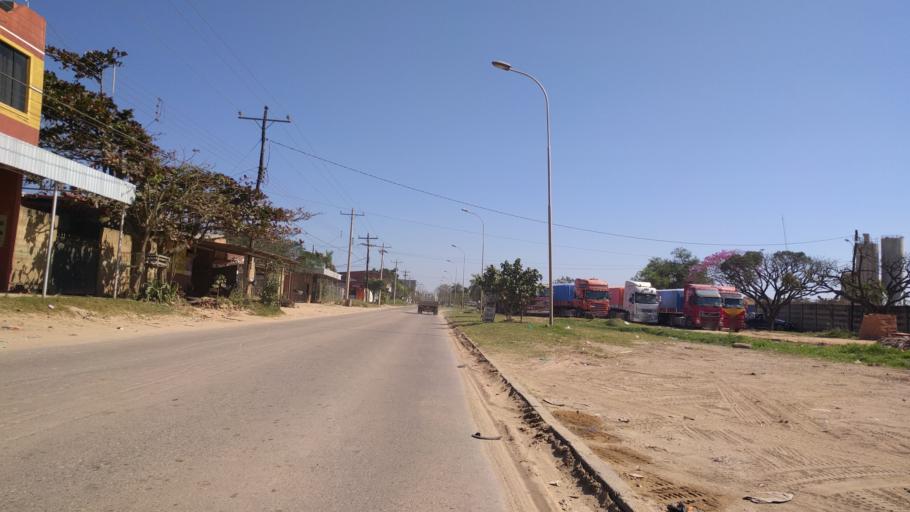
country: BO
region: Santa Cruz
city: Santa Cruz de la Sierra
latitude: -17.8519
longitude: -63.1994
